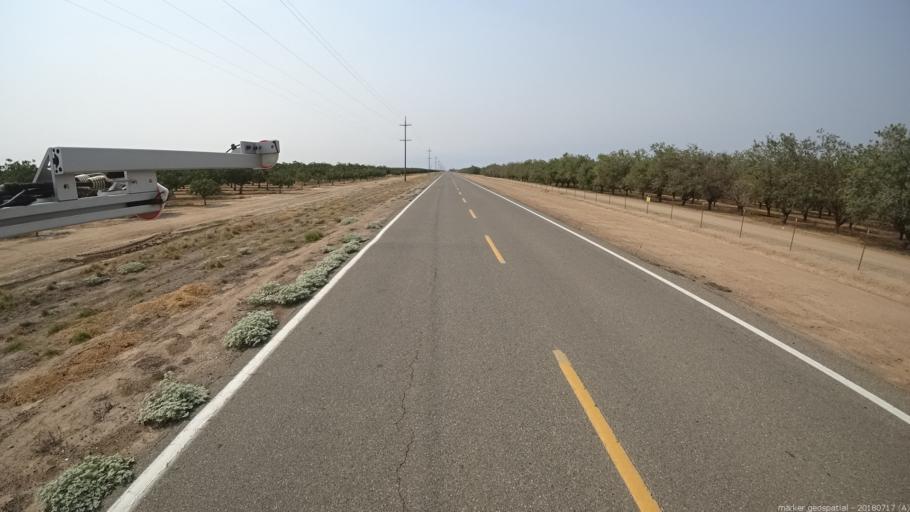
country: US
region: California
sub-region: Madera County
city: Fairmead
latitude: 37.1115
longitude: -120.1470
